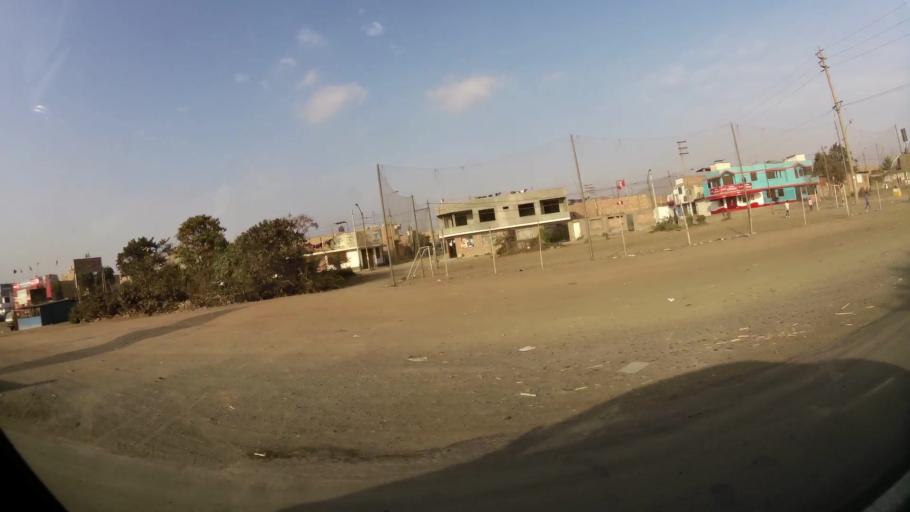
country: PE
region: Lima
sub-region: Lima
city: Santa Rosa
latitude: -11.7691
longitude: -77.1609
